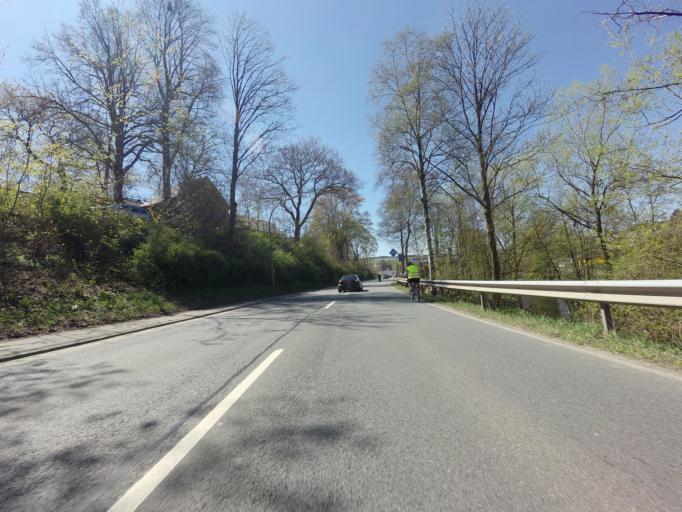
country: DE
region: North Rhine-Westphalia
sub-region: Regierungsbezirk Arnsberg
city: Erndtebruck
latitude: 50.9916
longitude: 8.2599
